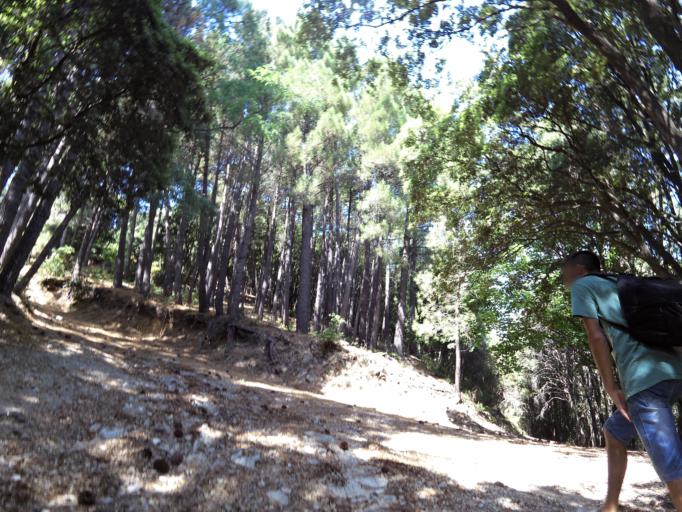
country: IT
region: Calabria
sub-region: Provincia di Reggio Calabria
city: Bivongi
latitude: 38.5120
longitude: 16.4310
